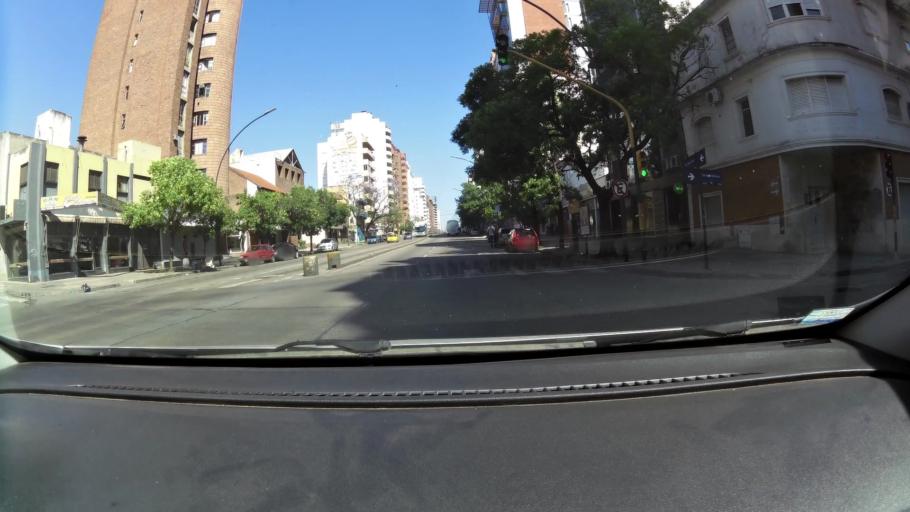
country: AR
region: Cordoba
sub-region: Departamento de Capital
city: Cordoba
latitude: -31.4190
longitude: -64.1929
